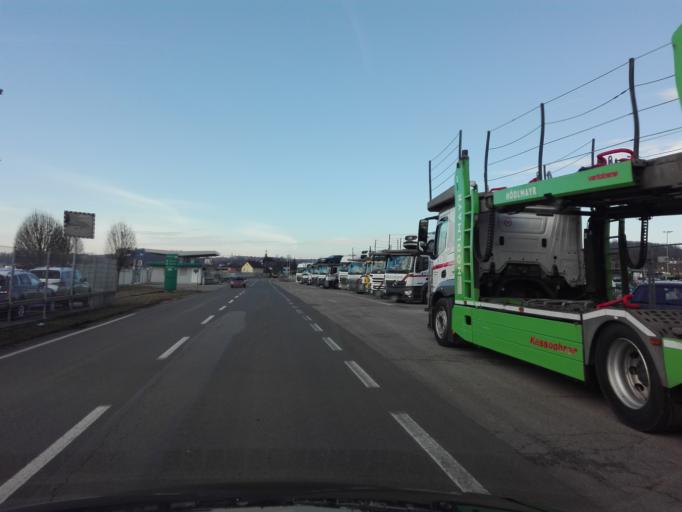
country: AT
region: Upper Austria
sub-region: Politischer Bezirk Perg
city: Perg
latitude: 48.2636
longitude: 14.5765
